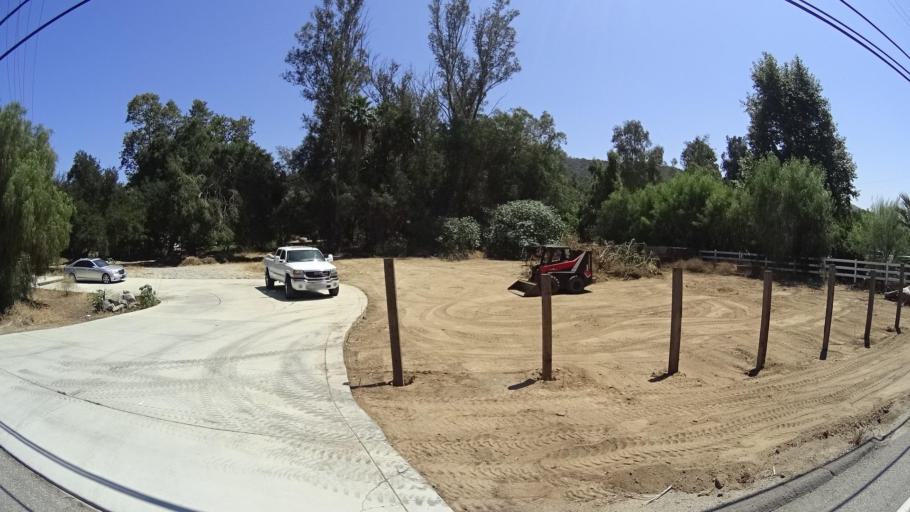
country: US
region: California
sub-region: San Diego County
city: Bonsall
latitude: 33.3302
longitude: -117.1913
